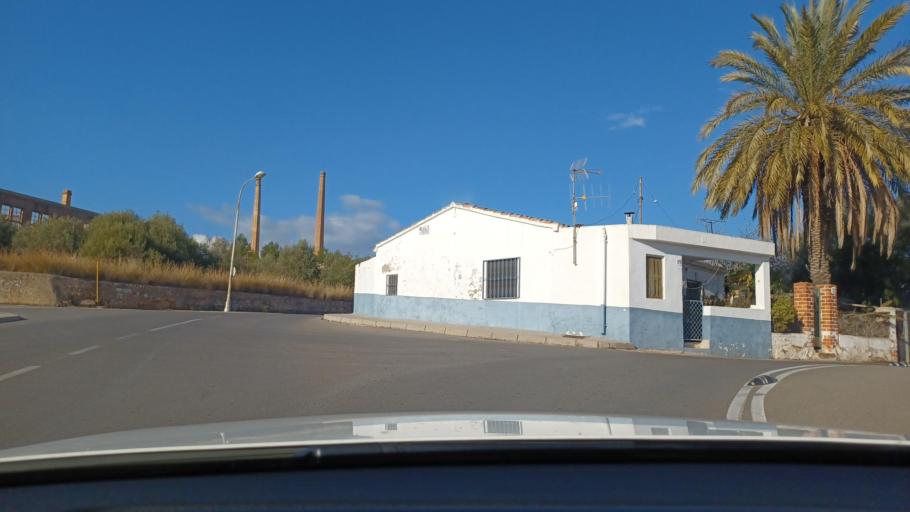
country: ES
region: Valencia
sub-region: Provincia de Castello
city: Onda
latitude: 39.9606
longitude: -0.2548
